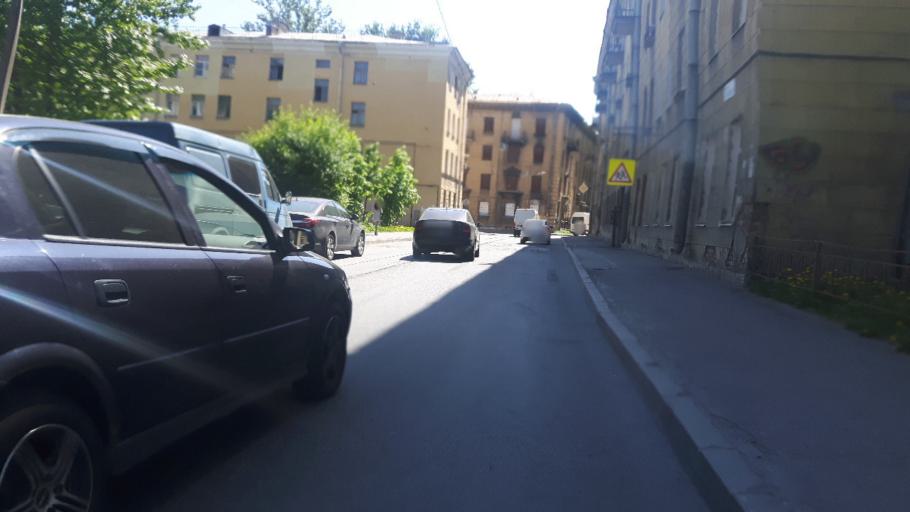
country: RU
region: St.-Petersburg
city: Admiralteisky
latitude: 59.9002
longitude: 30.2864
